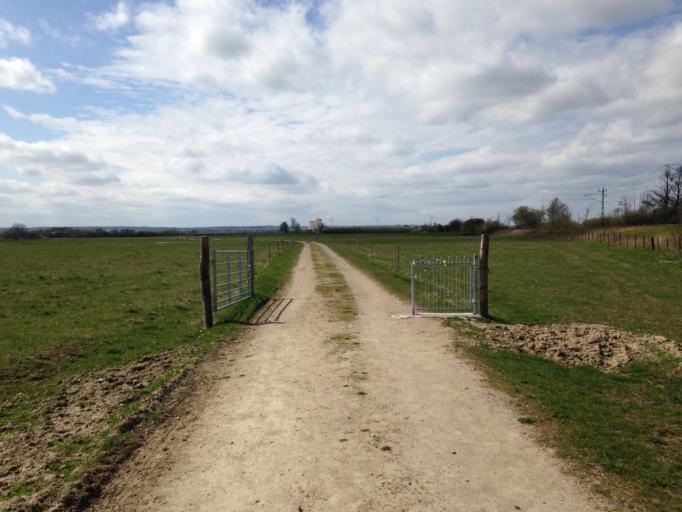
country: SE
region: Skane
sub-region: Kristianstads Kommun
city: Kristianstad
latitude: 56.0419
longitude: 14.1351
